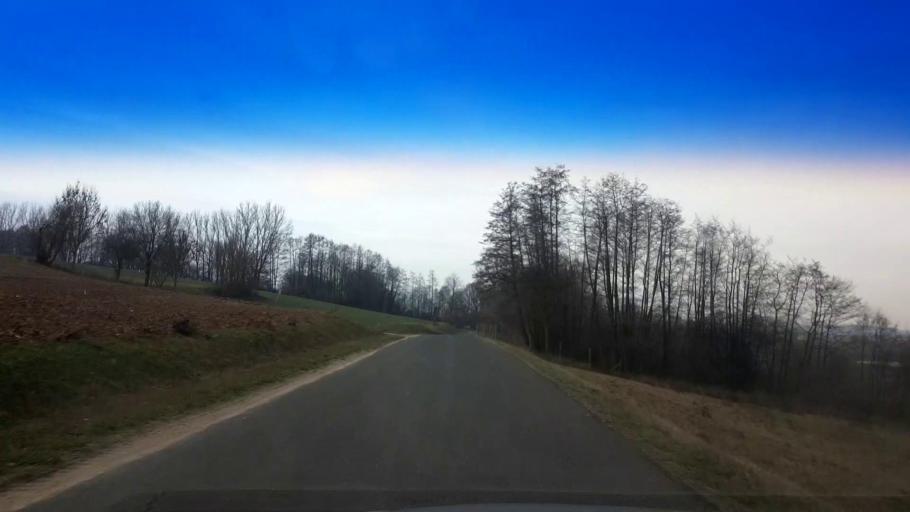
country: DE
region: Bavaria
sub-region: Upper Franconia
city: Hirschaid
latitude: 49.7992
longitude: 10.9931
